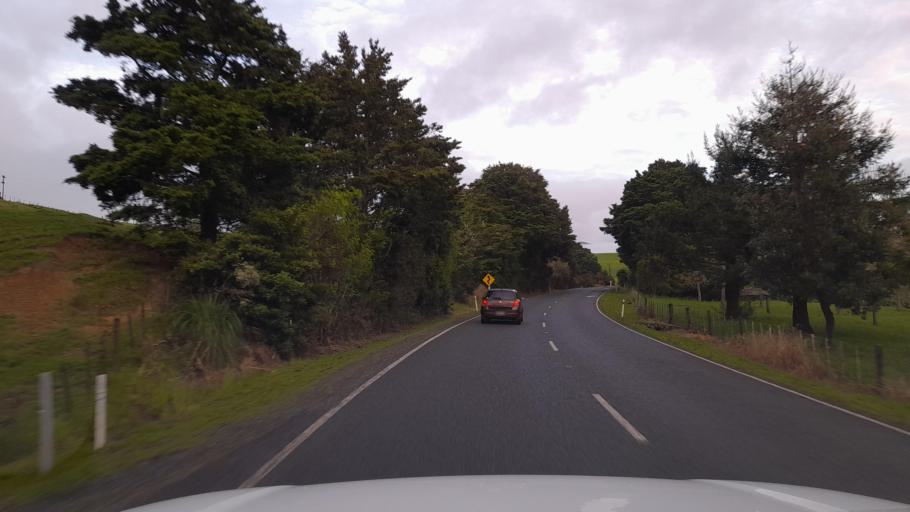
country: NZ
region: Northland
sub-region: Whangarei
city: Maungatapere
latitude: -35.7104
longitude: 174.0022
